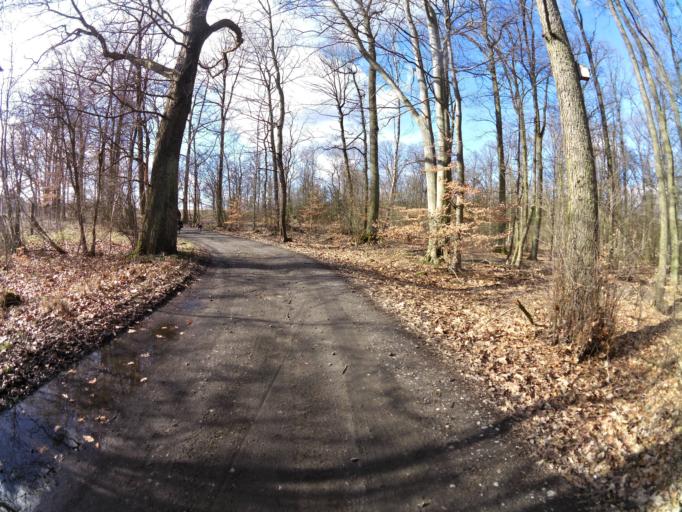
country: PL
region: West Pomeranian Voivodeship
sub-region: Powiat mysliborski
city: Debno
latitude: 52.7617
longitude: 14.7162
